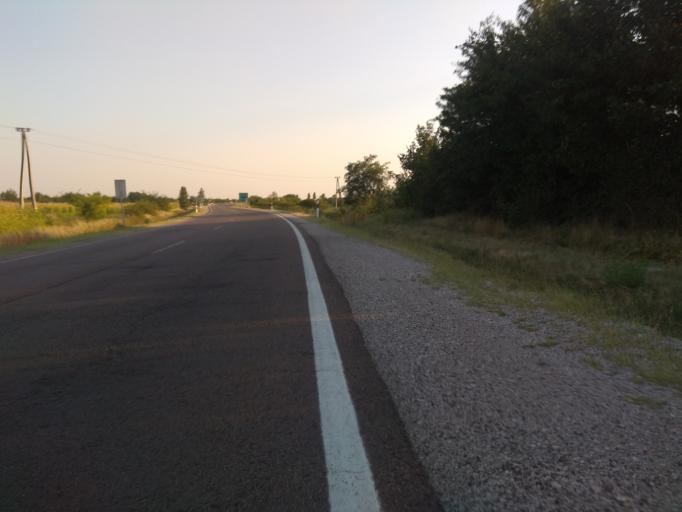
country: HU
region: Borsod-Abauj-Zemplen
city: Emod
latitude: 47.9451
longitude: 20.8309
